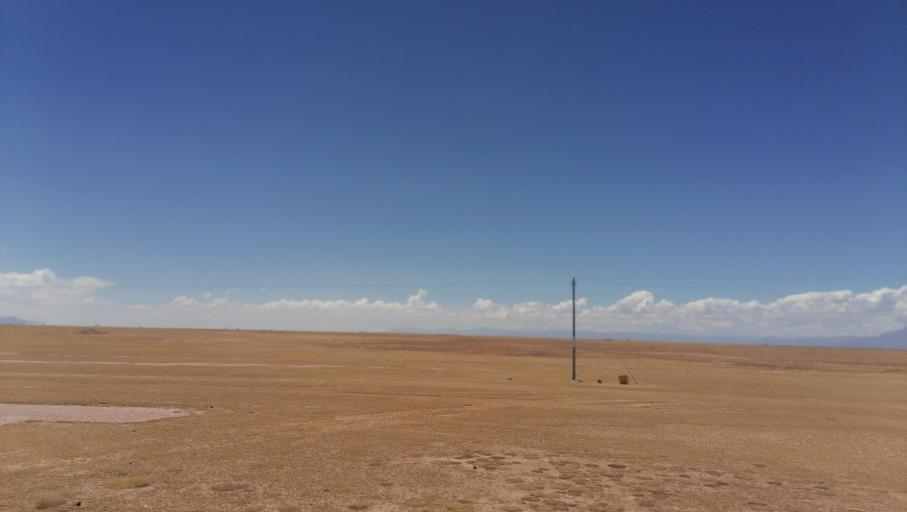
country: BO
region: Oruro
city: Challapata
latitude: -19.2237
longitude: -66.9718
